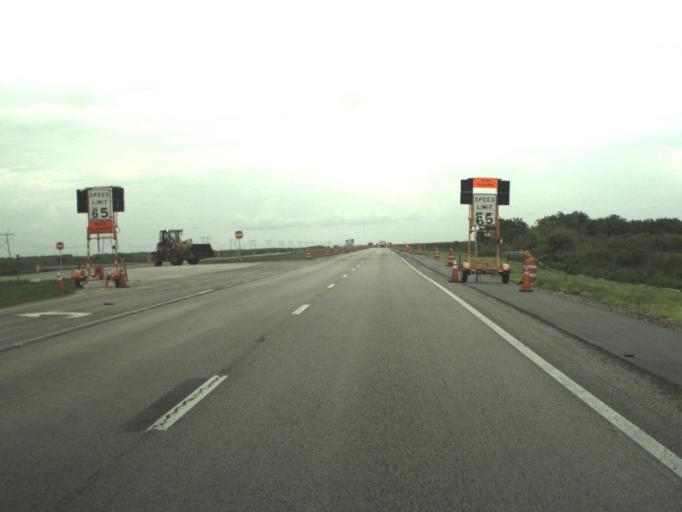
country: US
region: Florida
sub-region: Palm Beach County
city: Loxahatchee Groves
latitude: 26.7139
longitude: -80.4242
